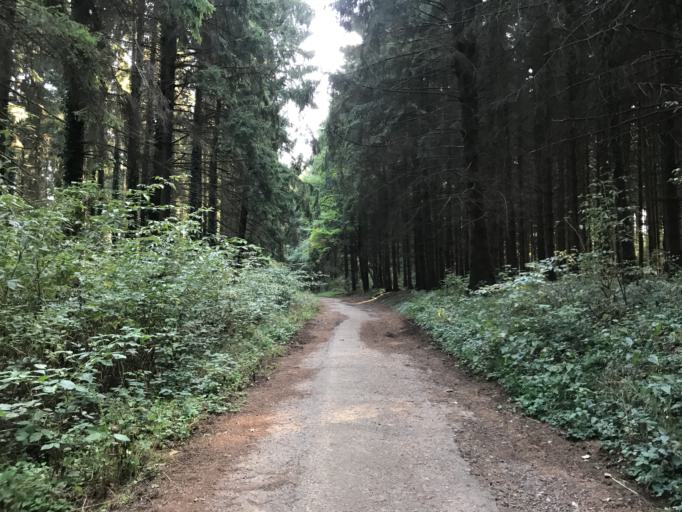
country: LU
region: Luxembourg
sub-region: Canton d'Esch-sur-Alzette
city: Niedercorn
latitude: 49.5359
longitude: 5.8736
